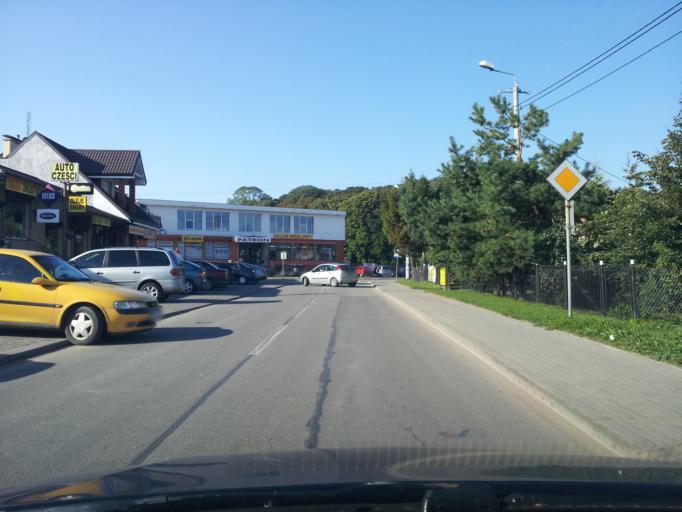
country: PL
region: Kujawsko-Pomorskie
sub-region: Powiat brodnicki
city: Swiedziebnia
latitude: 53.1528
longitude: 19.5601
